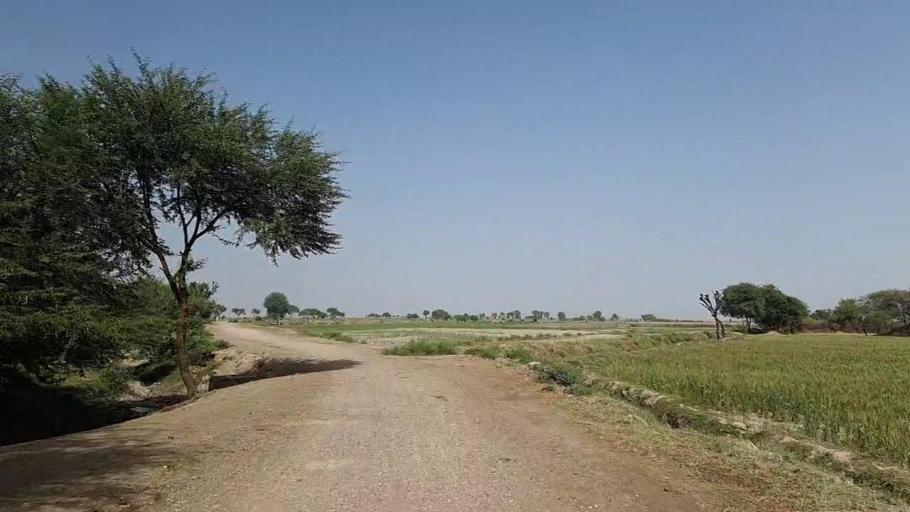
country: PK
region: Sindh
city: Jati
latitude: 24.3471
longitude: 68.3073
